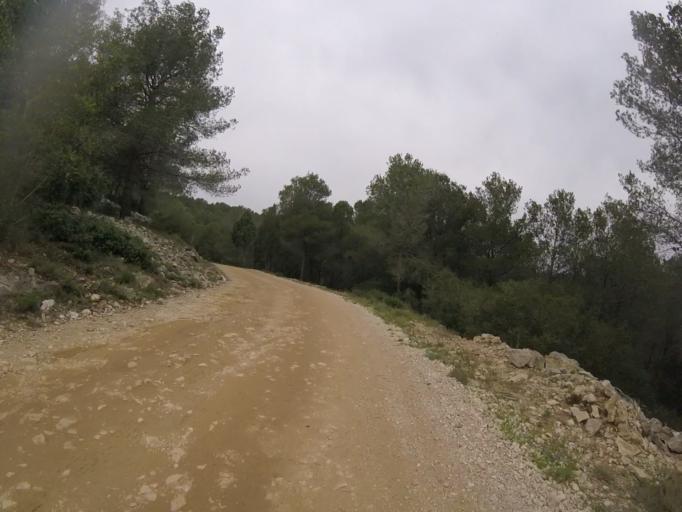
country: ES
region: Valencia
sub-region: Provincia de Castello
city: Alcala de Xivert
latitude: 40.3029
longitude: 0.2569
